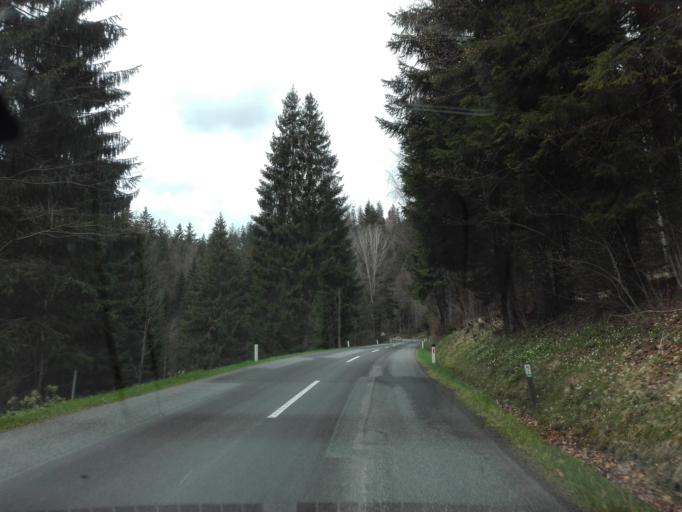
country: AT
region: Upper Austria
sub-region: Politischer Bezirk Rohrbach
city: Ulrichsberg
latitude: 48.7211
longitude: 13.8957
